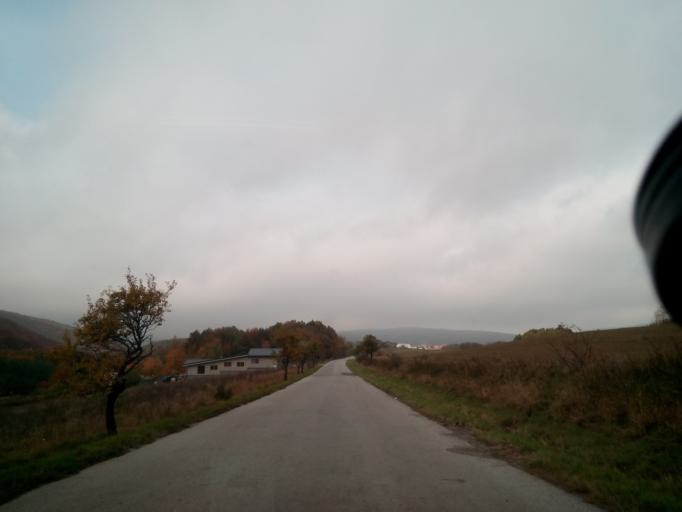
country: SK
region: Kosicky
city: Kosice
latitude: 48.7309
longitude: 21.1337
